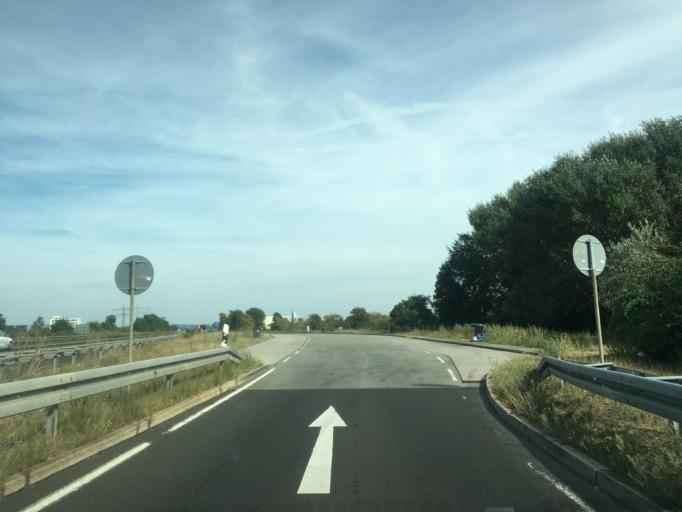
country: DE
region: Baden-Wuerttemberg
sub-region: Karlsruhe Region
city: Neulussheim
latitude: 49.3308
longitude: 8.5178
